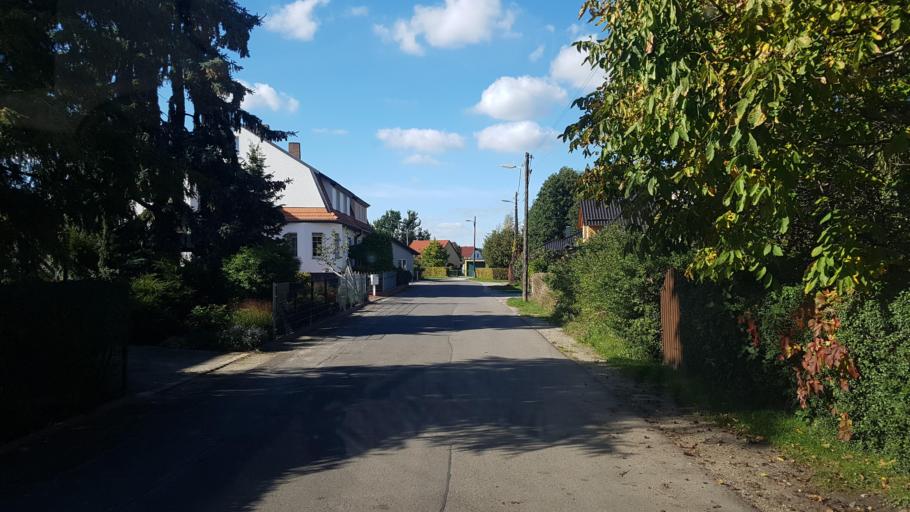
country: DE
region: Brandenburg
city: Cottbus
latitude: 51.7570
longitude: 14.2981
